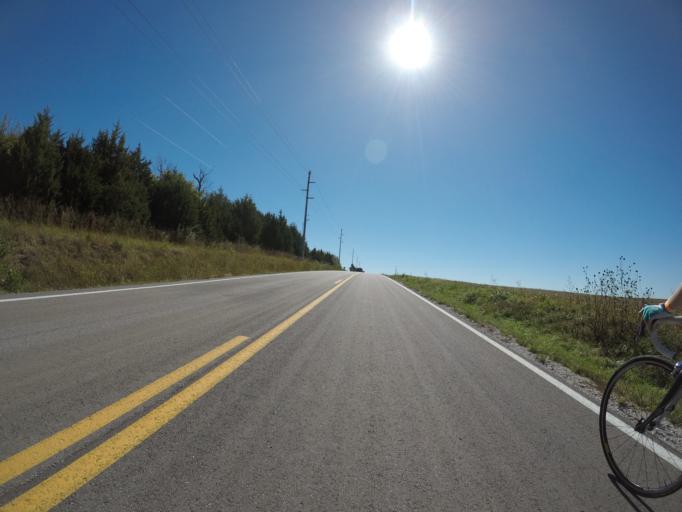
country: US
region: Kansas
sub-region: Johnson County
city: De Soto
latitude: 38.9514
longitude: -95.0195
